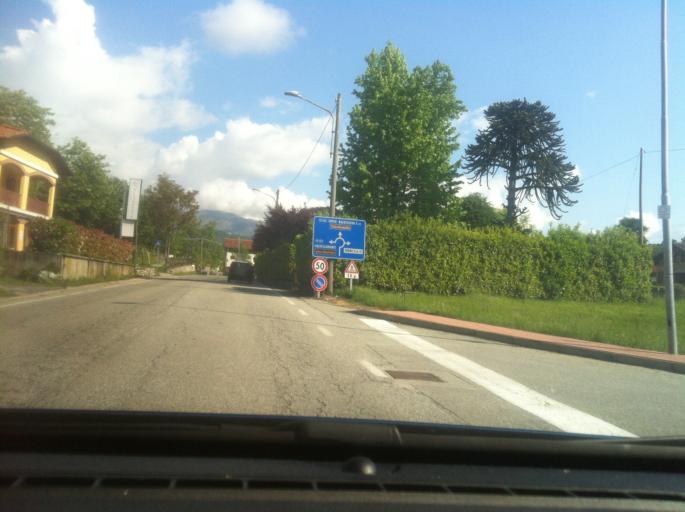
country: IT
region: Piedmont
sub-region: Provincia di Torino
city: Torre Canavese
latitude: 45.3919
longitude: 7.7574
